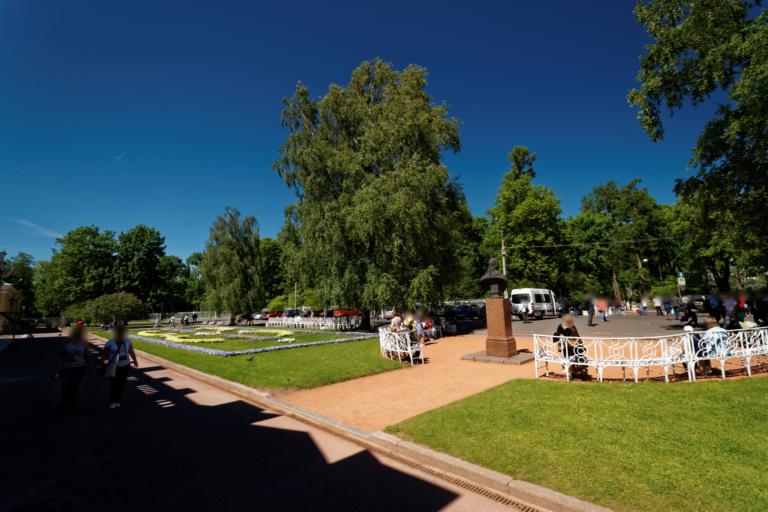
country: RU
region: St.-Petersburg
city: Pushkin
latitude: 59.7175
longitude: 30.3956
